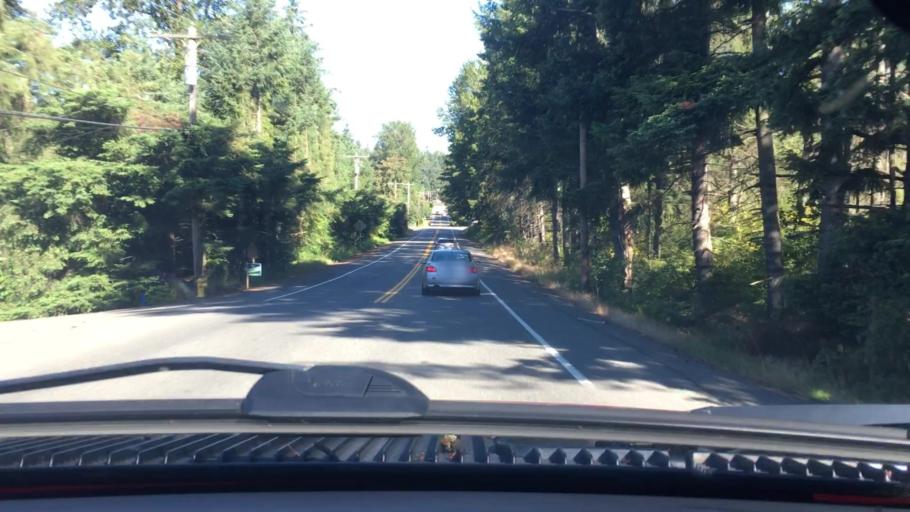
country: US
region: Washington
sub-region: King County
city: Covington
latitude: 47.3416
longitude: -122.1314
